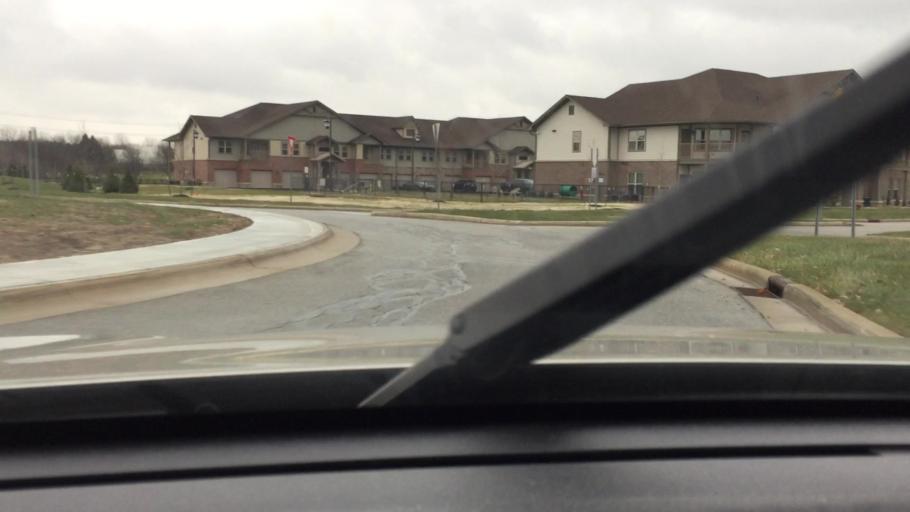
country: US
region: Indiana
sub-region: Hamilton County
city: Carmel
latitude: 40.0075
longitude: -86.0922
